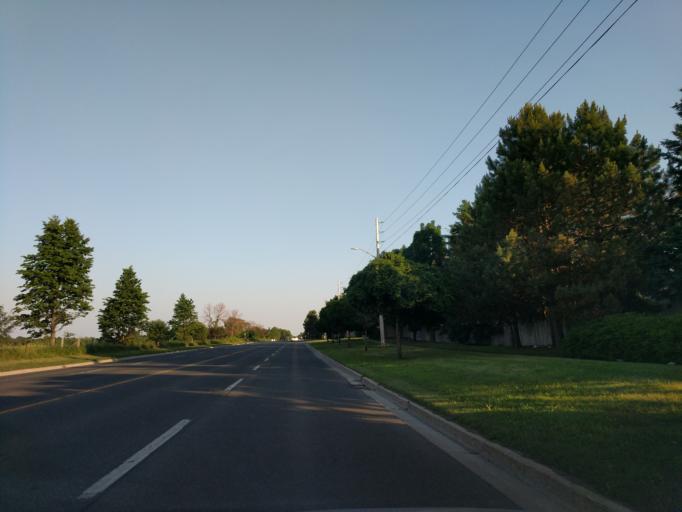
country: CA
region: Ontario
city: Oshawa
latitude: 43.9161
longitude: -78.9039
